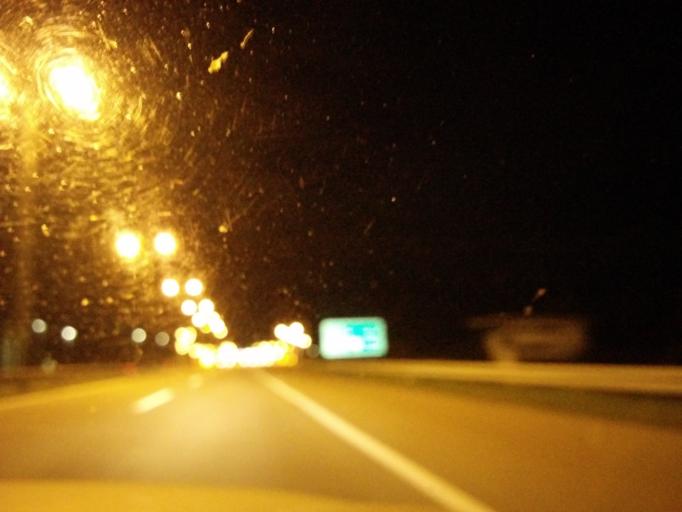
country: RS
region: Autonomna Pokrajina Vojvodina
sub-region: Sremski Okrug
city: Sid
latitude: 45.0483
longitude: 19.1991
